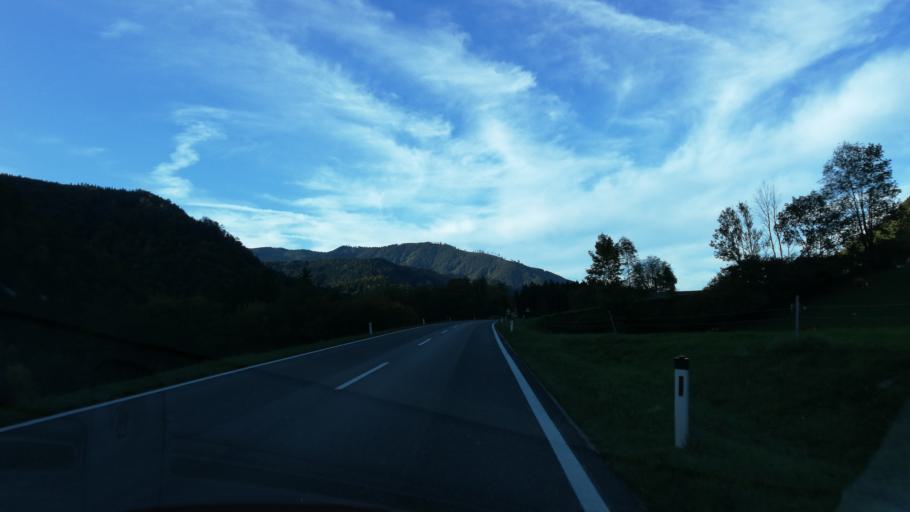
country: AT
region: Styria
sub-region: Politischer Bezirk Liezen
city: Altenmarkt bei Sankt Gallen
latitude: 47.7854
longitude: 14.6480
